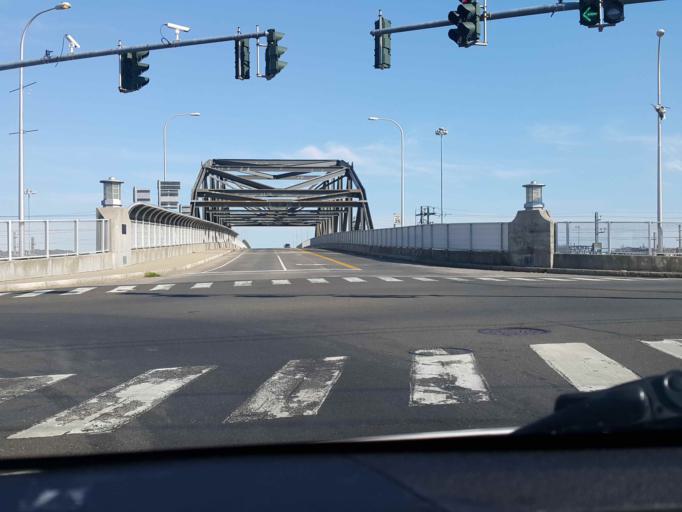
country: US
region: Connecticut
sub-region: New Haven County
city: New Haven
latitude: 41.2964
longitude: -72.9284
